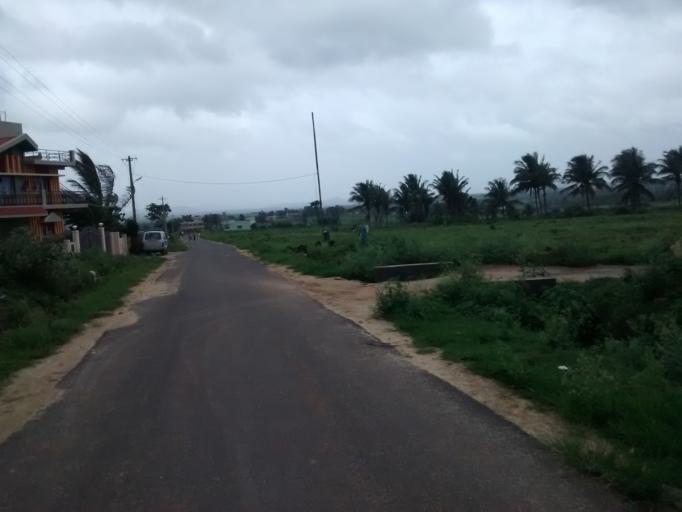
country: IN
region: Karnataka
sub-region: Hassan
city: Hassan
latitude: 12.9524
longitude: 76.1316
